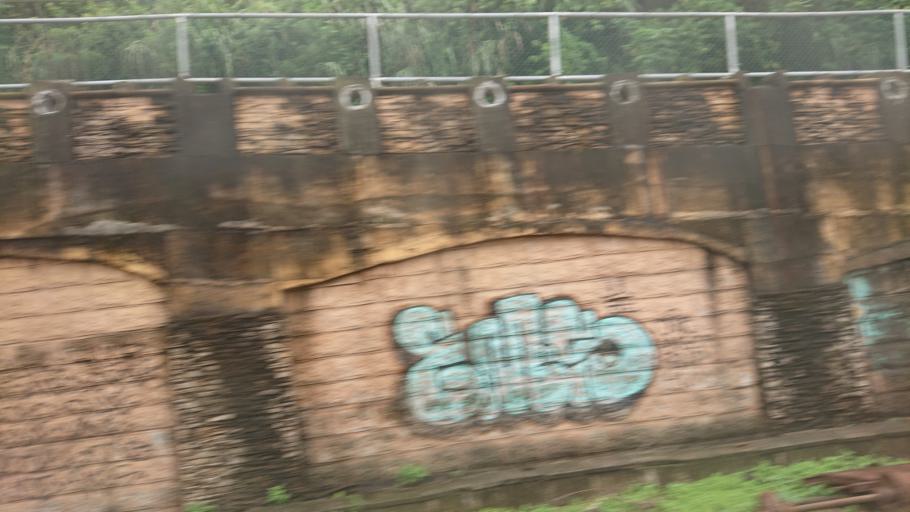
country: TW
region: Taiwan
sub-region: Keelung
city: Keelung
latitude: 25.0824
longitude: 121.7038
